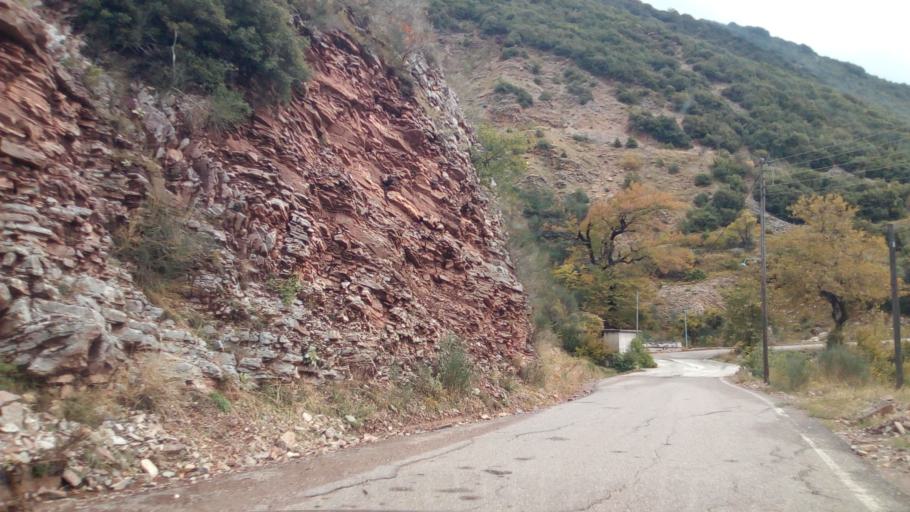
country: GR
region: West Greece
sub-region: Nomos Aitolias kai Akarnanias
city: Nafpaktos
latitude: 38.5300
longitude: 21.8311
